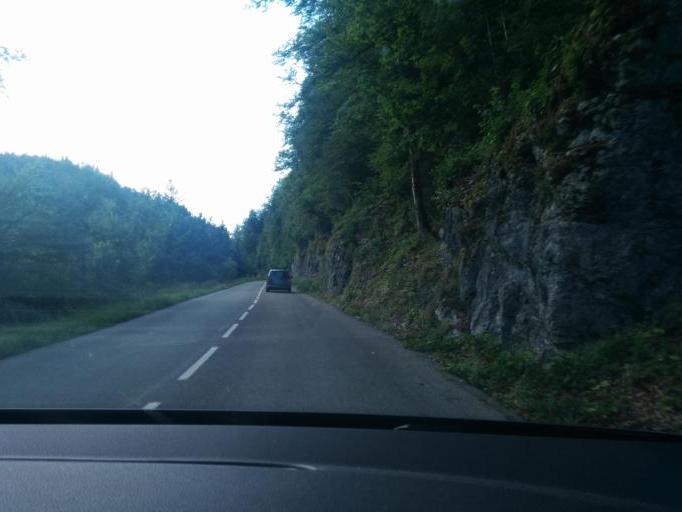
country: FR
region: Franche-Comte
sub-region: Departement du Jura
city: Saint-Lupicin
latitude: 46.4426
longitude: 5.8091
